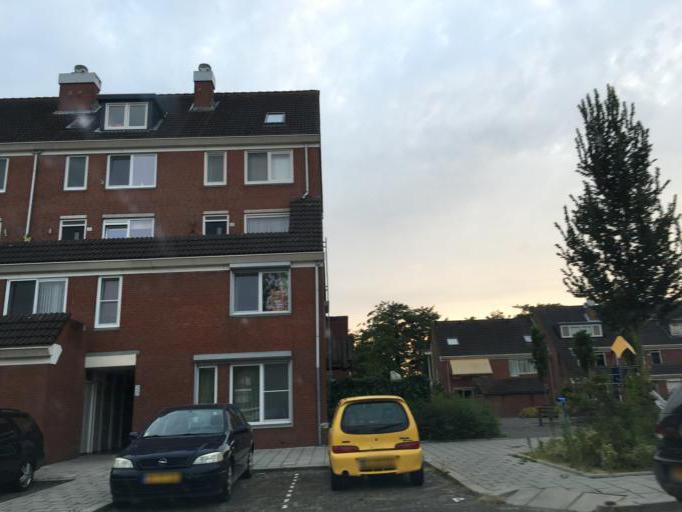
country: NL
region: South Holland
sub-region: Gemeente Capelle aan den IJssel
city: Capelle aan den IJssel
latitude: 51.9521
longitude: 4.5771
